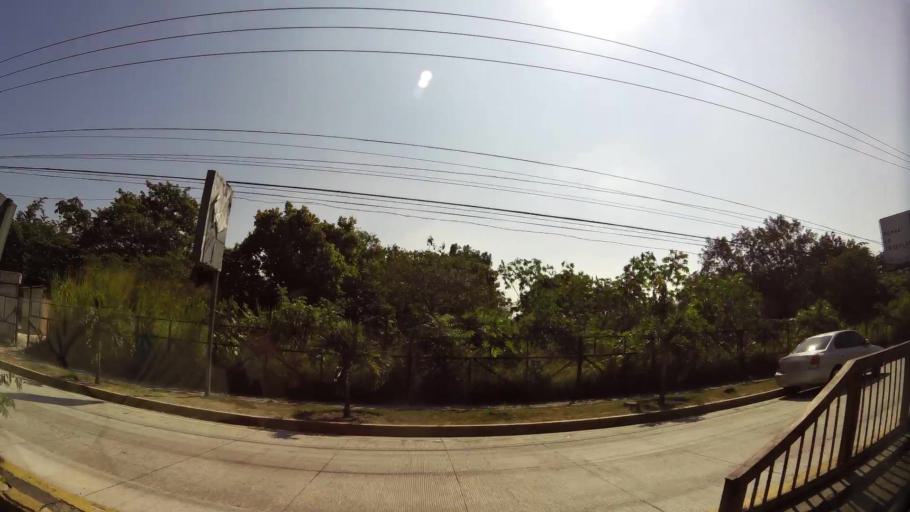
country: SV
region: La Libertad
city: Antiguo Cuscatlan
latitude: 13.6757
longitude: -89.2525
